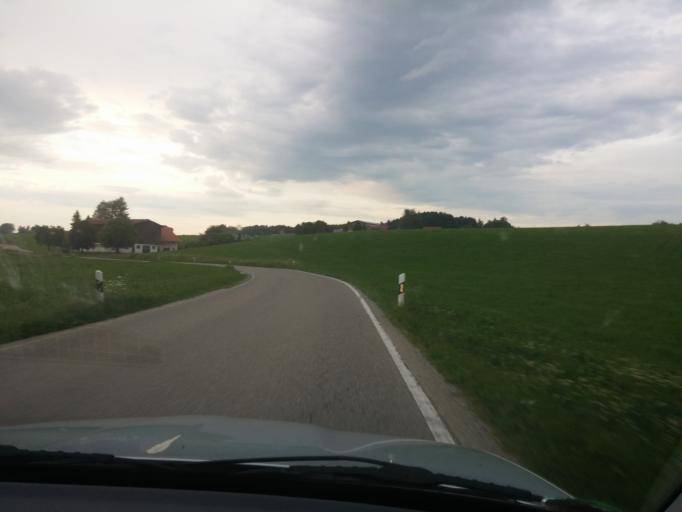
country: DE
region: Bavaria
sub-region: Swabia
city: Legau
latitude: 47.8292
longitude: 10.1016
